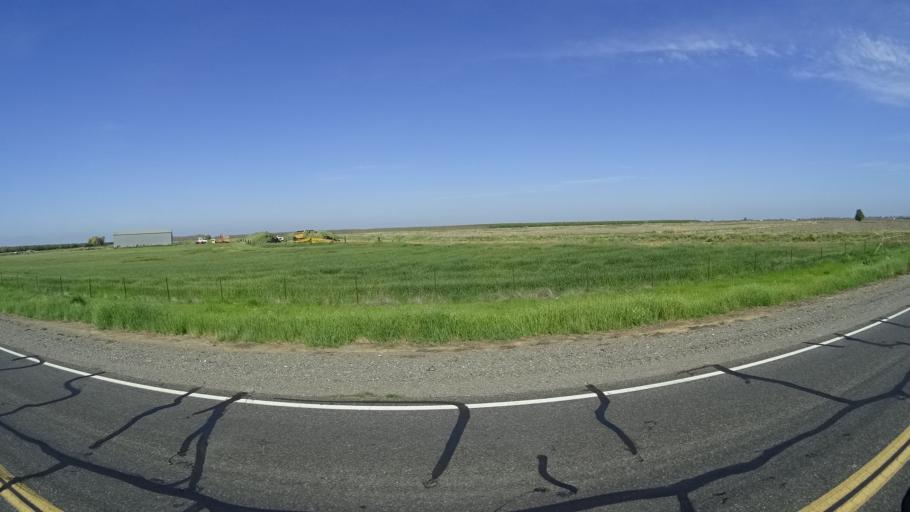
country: US
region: California
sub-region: Glenn County
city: Hamilton City
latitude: 39.6736
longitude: -122.0068
